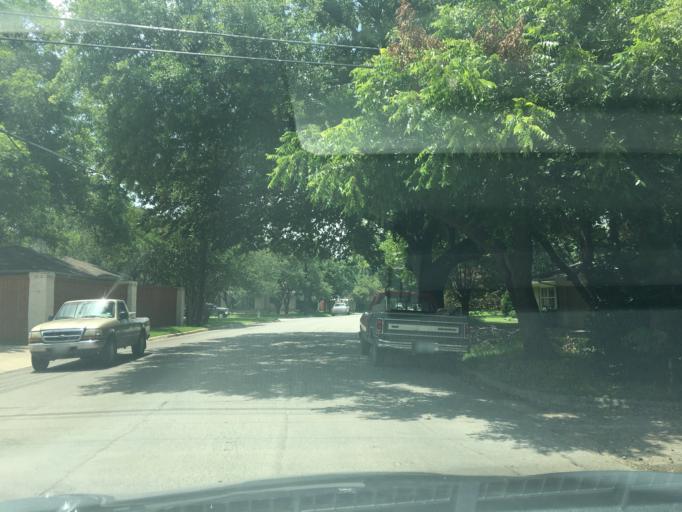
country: US
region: Texas
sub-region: Dallas County
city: University Park
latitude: 32.8788
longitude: -96.7903
